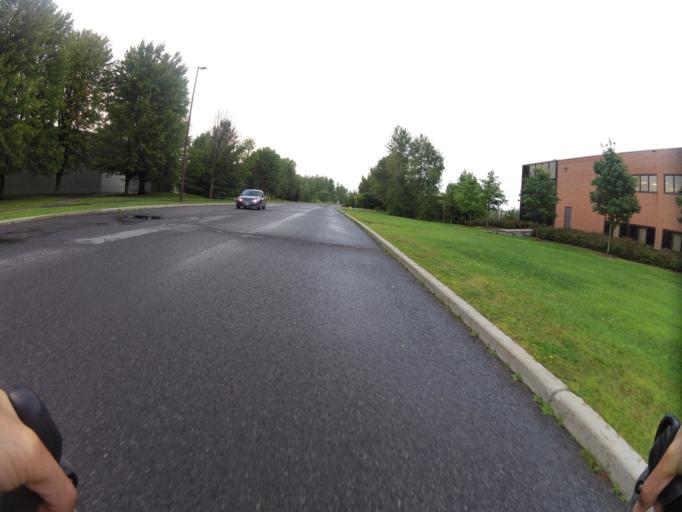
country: CA
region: Ontario
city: Bells Corners
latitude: 45.3452
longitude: -75.9143
